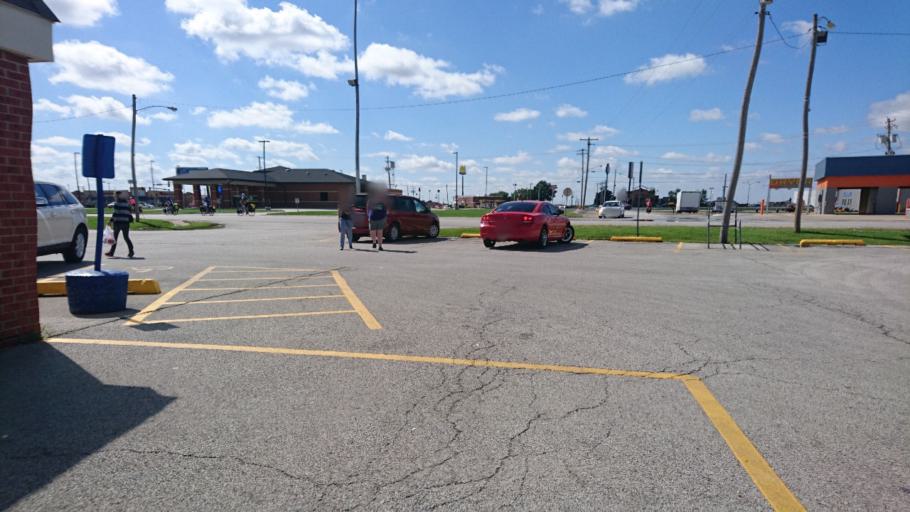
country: US
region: Illinois
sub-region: Montgomery County
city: Litchfield
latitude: 39.1789
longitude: -89.6659
